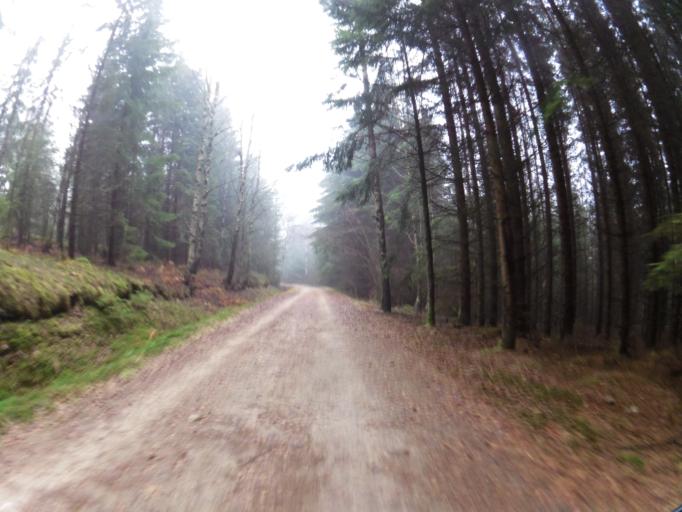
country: NO
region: Ostfold
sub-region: Fredrikstad
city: Fredrikstad
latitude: 59.2575
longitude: 10.9691
